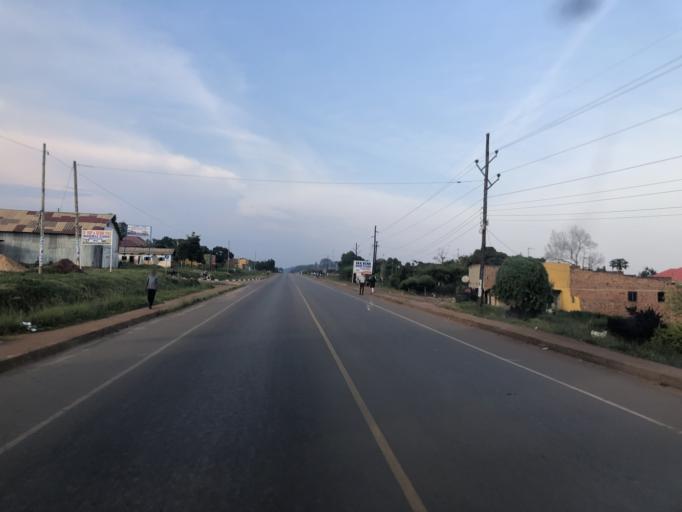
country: UG
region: Central Region
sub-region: Mpigi District
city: Mpigi
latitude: 0.2078
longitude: 32.3161
